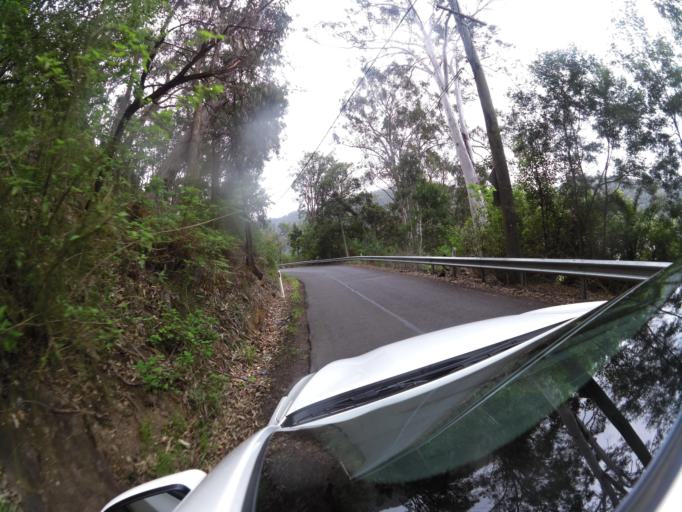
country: AU
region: New South Wales
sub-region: Hornsby Shire
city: Glenorie
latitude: -33.4141
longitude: 150.9631
